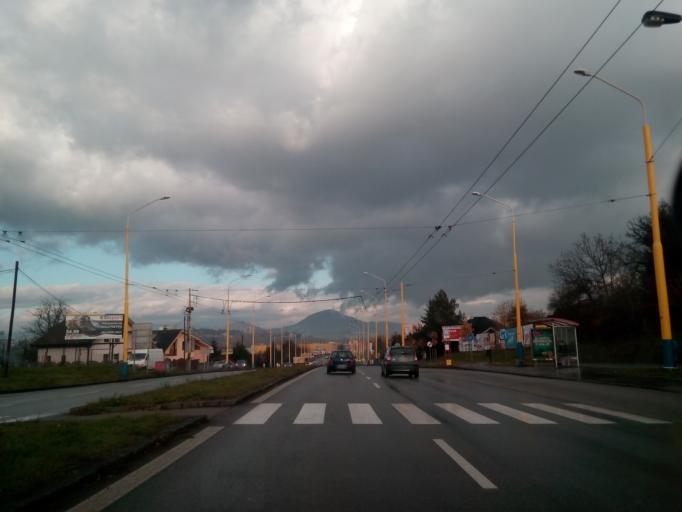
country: SK
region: Presovsky
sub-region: Okres Presov
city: Presov
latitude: 48.9789
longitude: 21.2640
